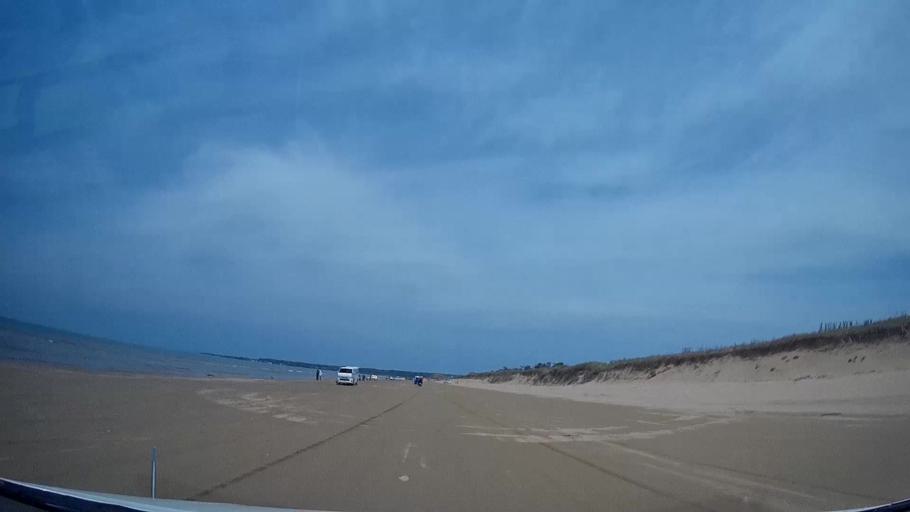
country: JP
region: Ishikawa
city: Hakui
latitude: 36.8819
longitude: 136.7628
